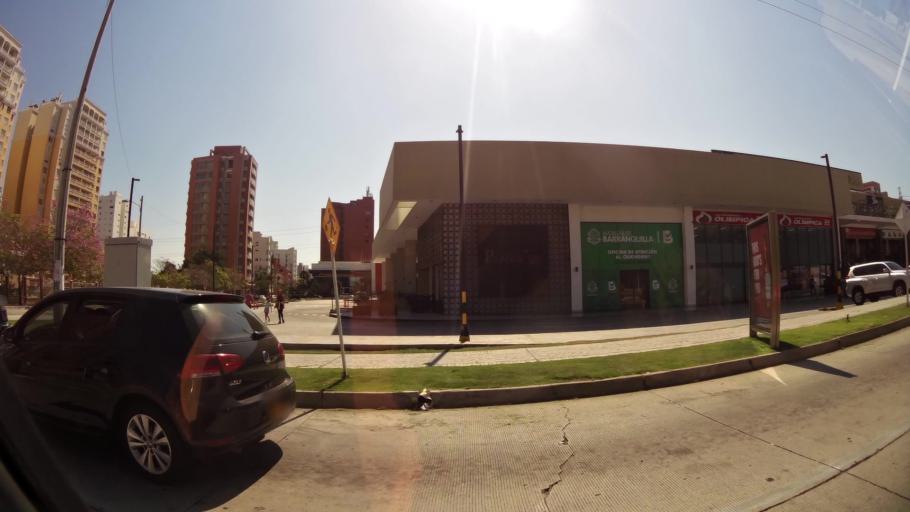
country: CO
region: Atlantico
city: Barranquilla
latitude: 11.0160
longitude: -74.8270
